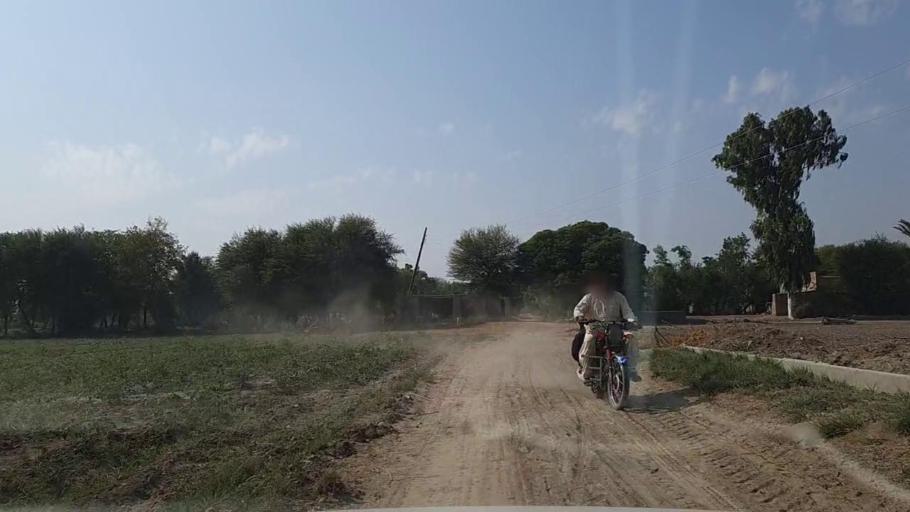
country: PK
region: Sindh
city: Mirpur Batoro
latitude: 24.6759
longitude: 68.3729
